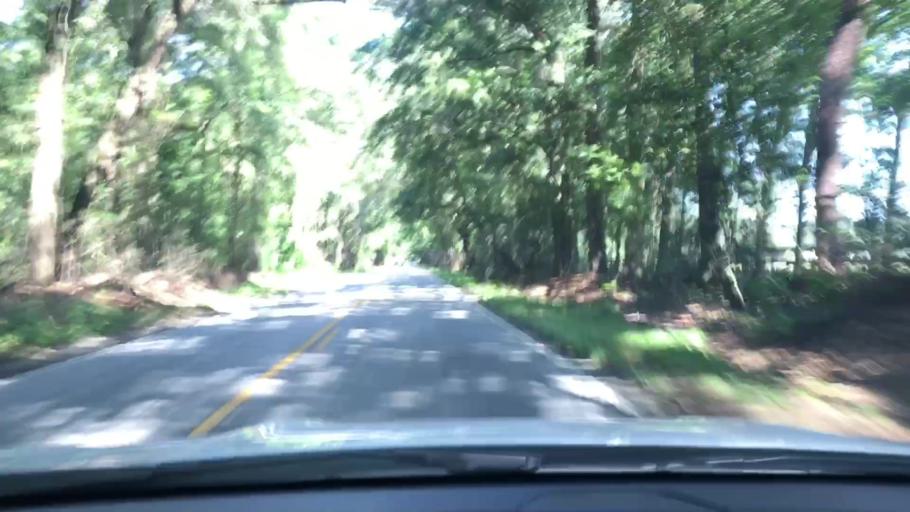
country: US
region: South Carolina
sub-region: Berkeley County
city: Ladson
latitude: 32.8914
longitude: -80.1298
